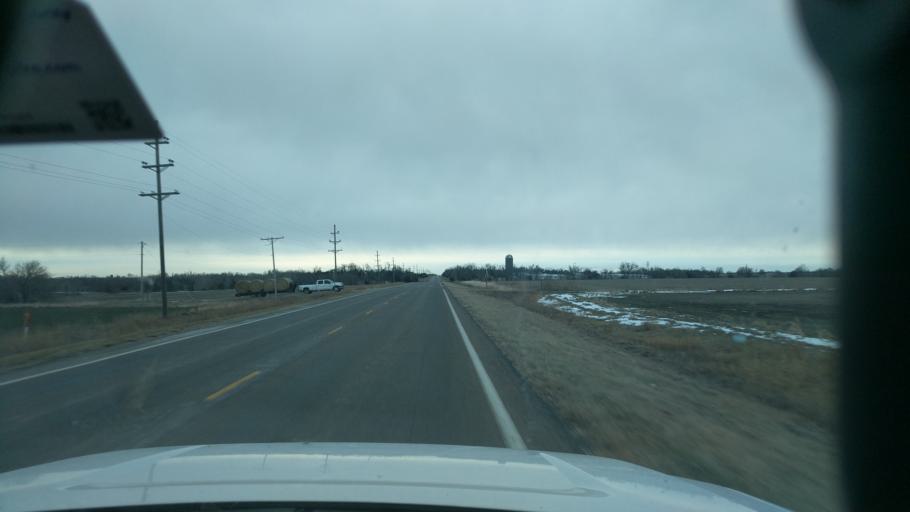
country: US
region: Kansas
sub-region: Marion County
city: Hillsboro
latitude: 38.3054
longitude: -97.3347
